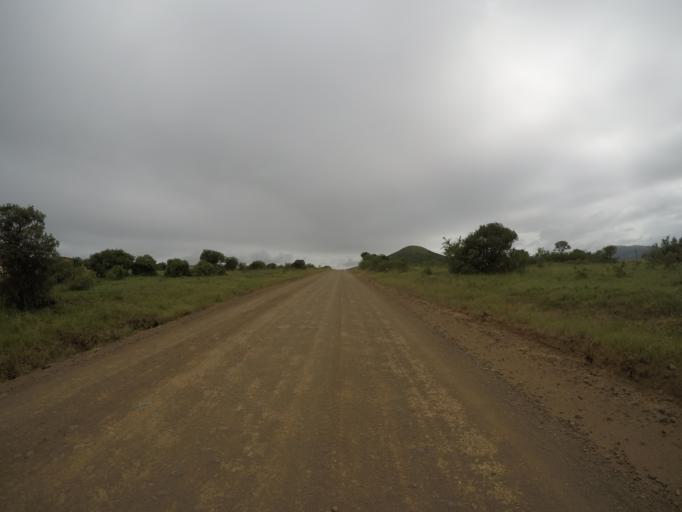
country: ZA
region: KwaZulu-Natal
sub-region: uThungulu District Municipality
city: Empangeni
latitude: -28.6092
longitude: 31.8466
